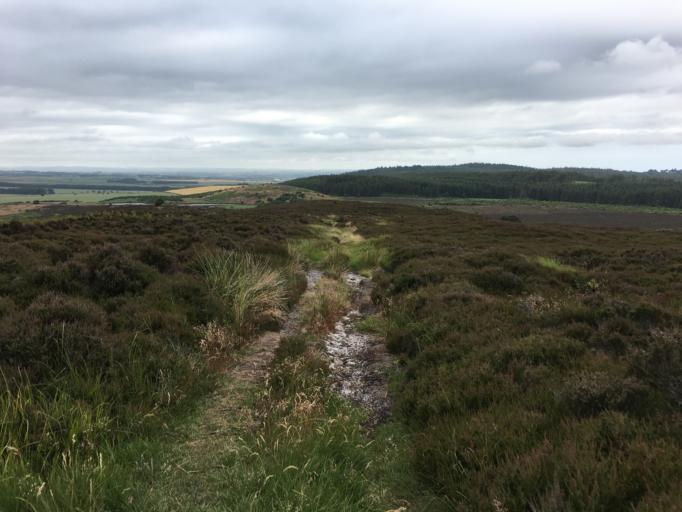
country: GB
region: England
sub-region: Northumberland
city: Lowick
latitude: 55.6173
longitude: -1.9145
